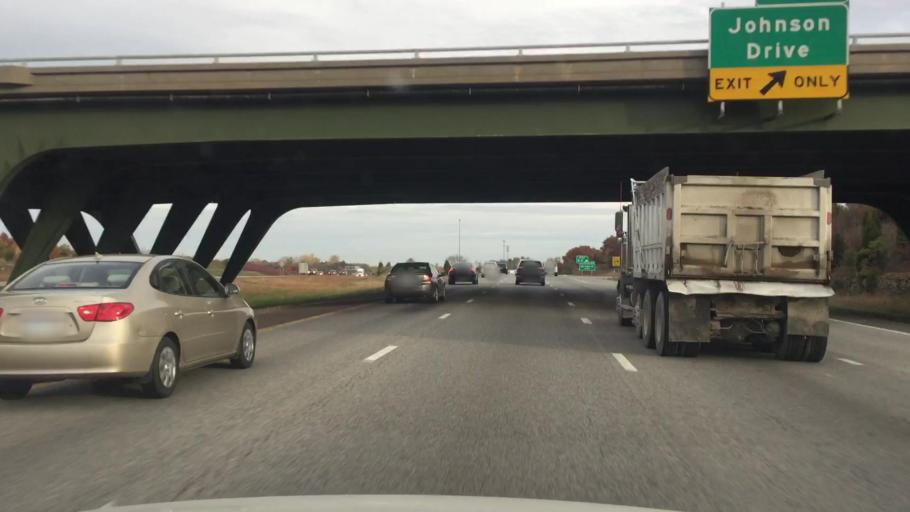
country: US
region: Kansas
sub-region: Wyandotte County
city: Edwardsville
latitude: 39.0215
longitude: -94.7852
